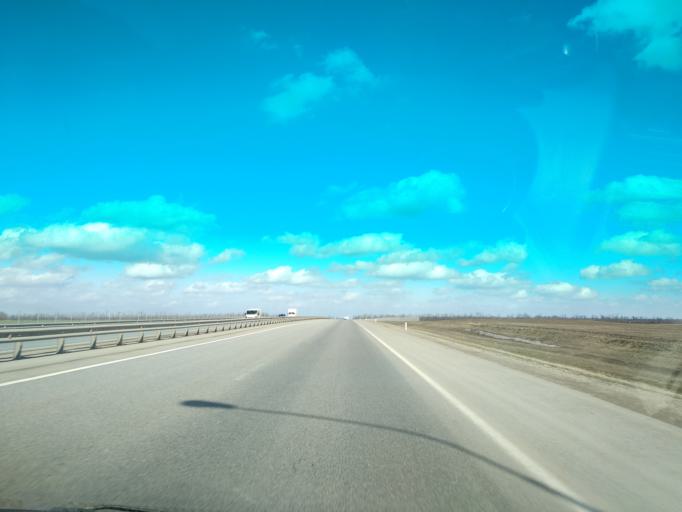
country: RU
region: Krasnodarskiy
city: Berezanskaya
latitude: 45.5895
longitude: 39.5188
